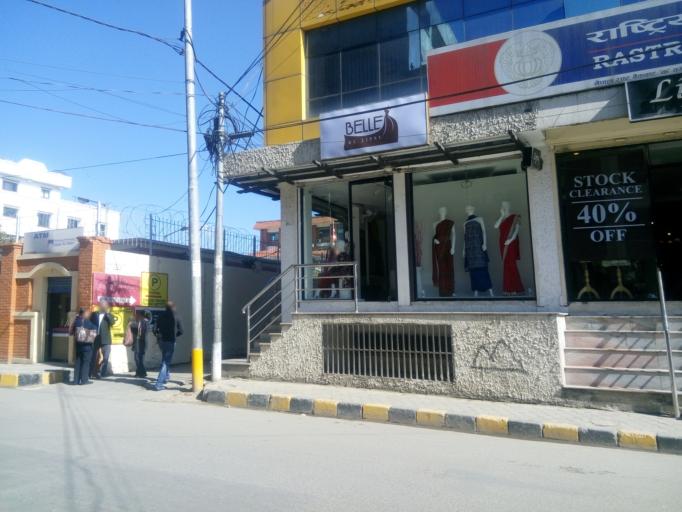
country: NP
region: Central Region
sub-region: Bagmati Zone
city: Kathmandu
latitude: 27.7180
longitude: 85.3306
